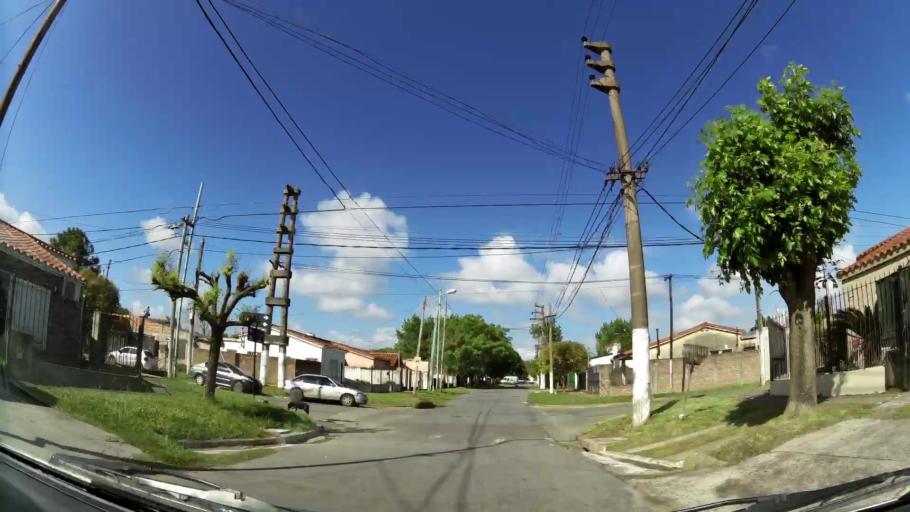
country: AR
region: Buenos Aires
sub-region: Partido de Quilmes
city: Quilmes
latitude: -34.7873
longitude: -58.1513
